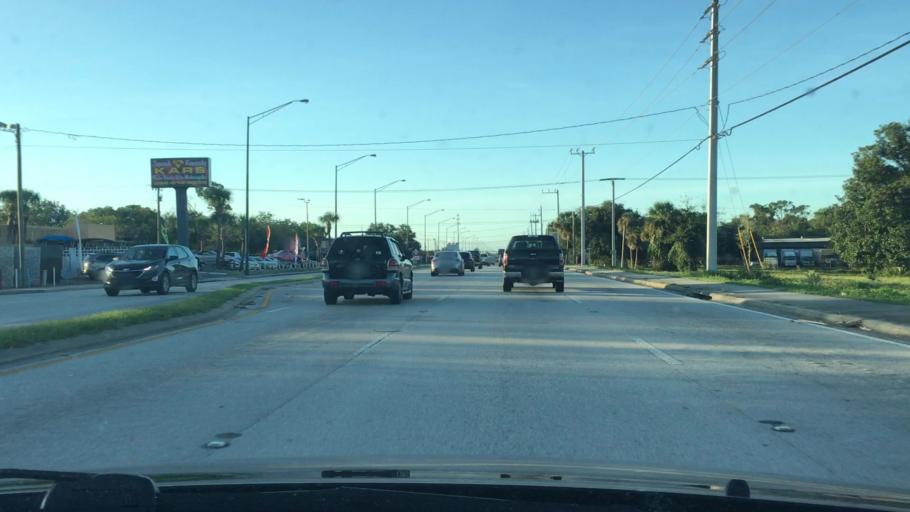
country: US
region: Florida
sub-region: Volusia County
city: Holly Hill
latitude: 29.2492
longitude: -81.0691
